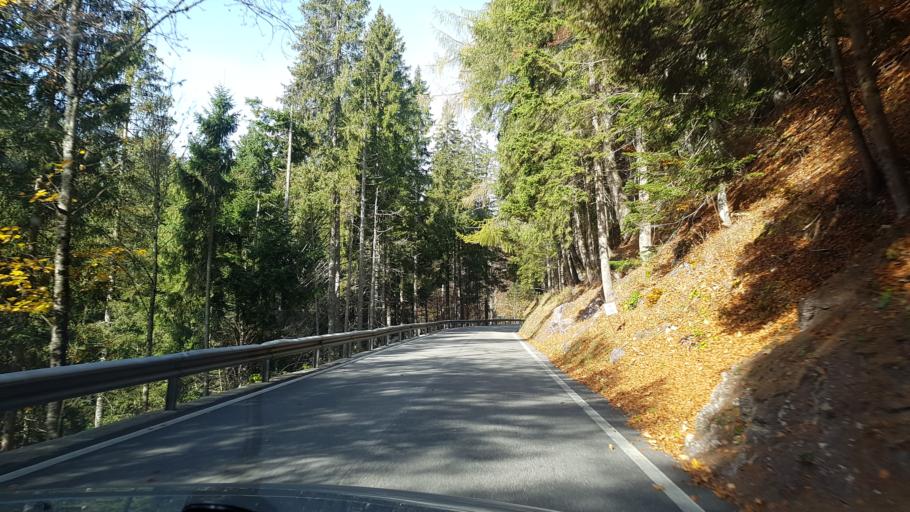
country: IT
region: Veneto
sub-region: Provincia di Belluno
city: Candide
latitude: 46.6424
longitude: 12.4553
